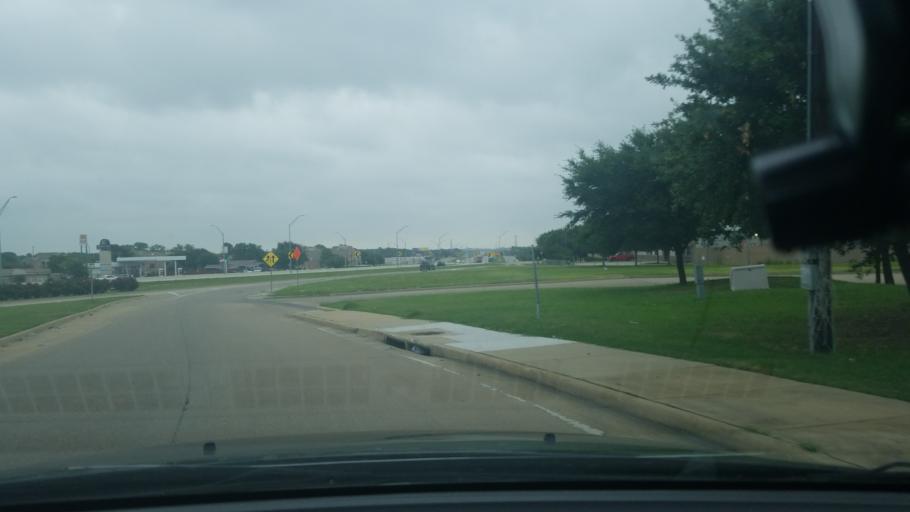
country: US
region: Texas
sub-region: Dallas County
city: Mesquite
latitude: 32.7922
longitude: -96.6551
